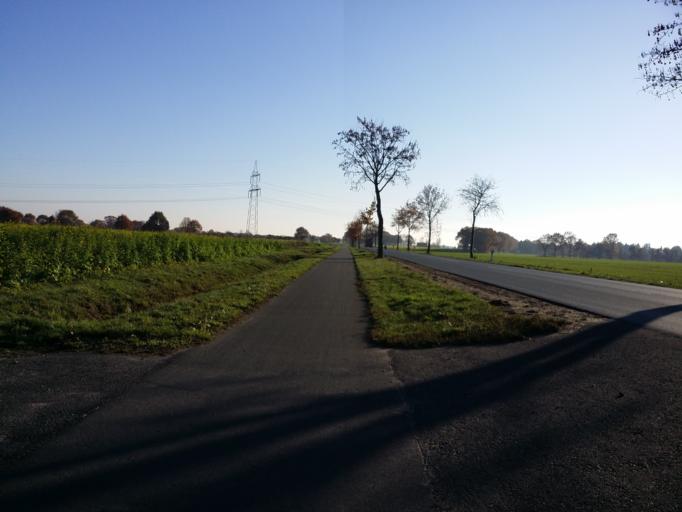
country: DE
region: Lower Saxony
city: Langwedel
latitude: 53.0244
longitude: 9.1644
